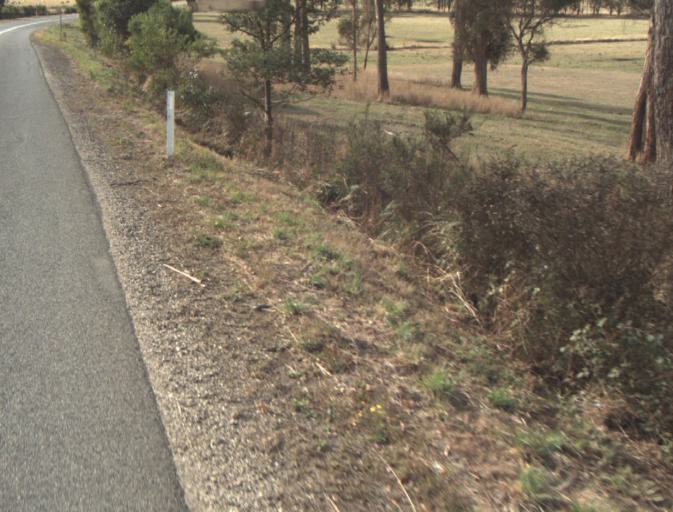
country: AU
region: Tasmania
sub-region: Launceston
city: Mayfield
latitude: -41.2250
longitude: 147.1225
